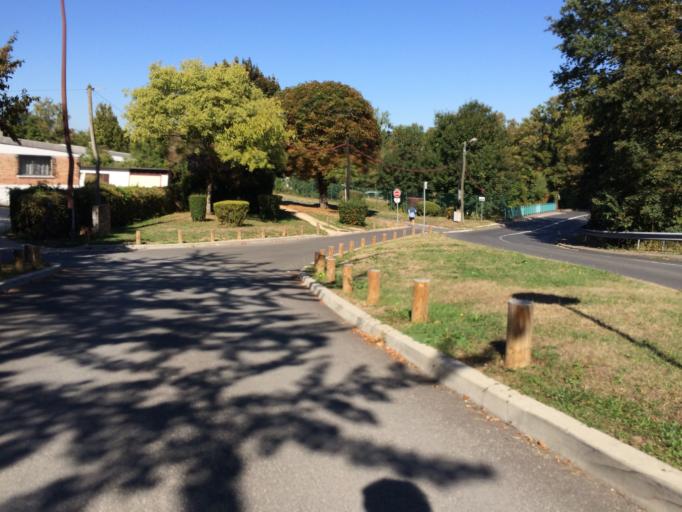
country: FR
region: Ile-de-France
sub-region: Departement de l'Essonne
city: Bures-sur-Yvette
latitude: 48.6955
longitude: 2.1693
